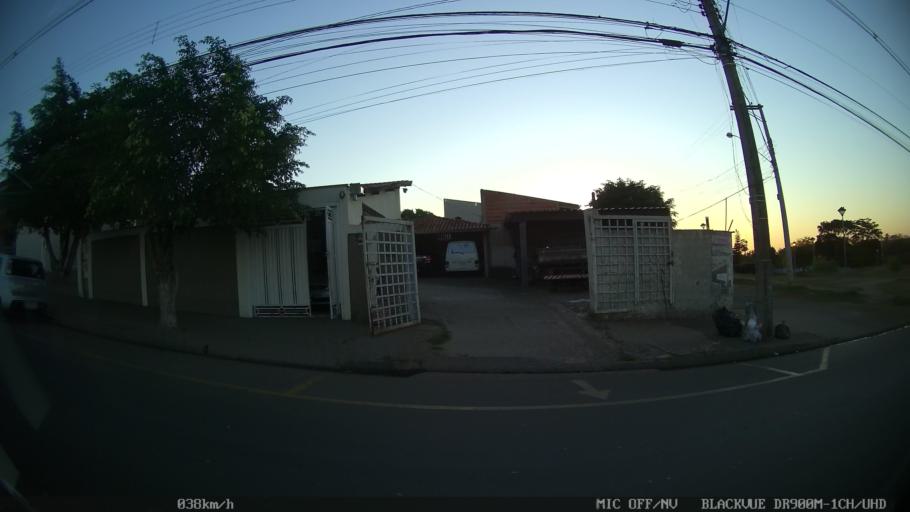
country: BR
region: Sao Paulo
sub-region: Sao Jose Do Rio Preto
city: Sao Jose do Rio Preto
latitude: -20.7871
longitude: -49.3439
